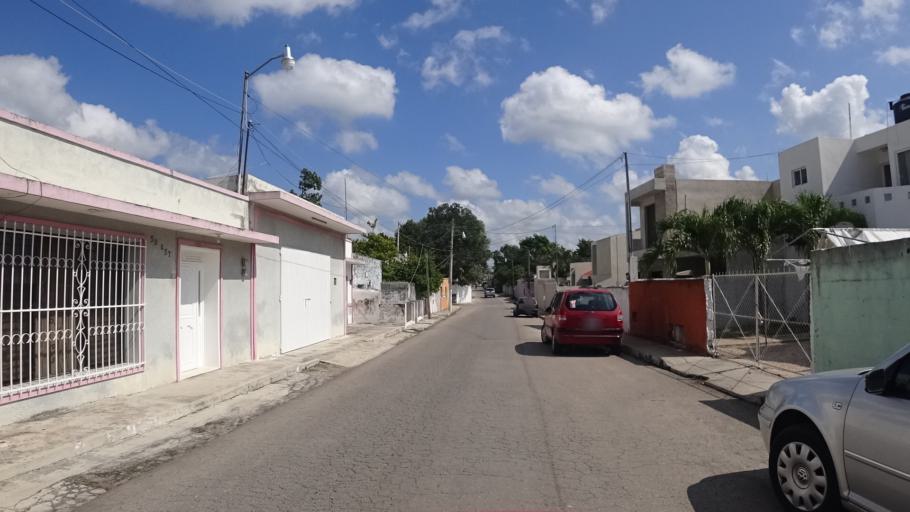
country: MX
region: Yucatan
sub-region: Tizimin
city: Tizimin
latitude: 21.1353
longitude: -88.1538
